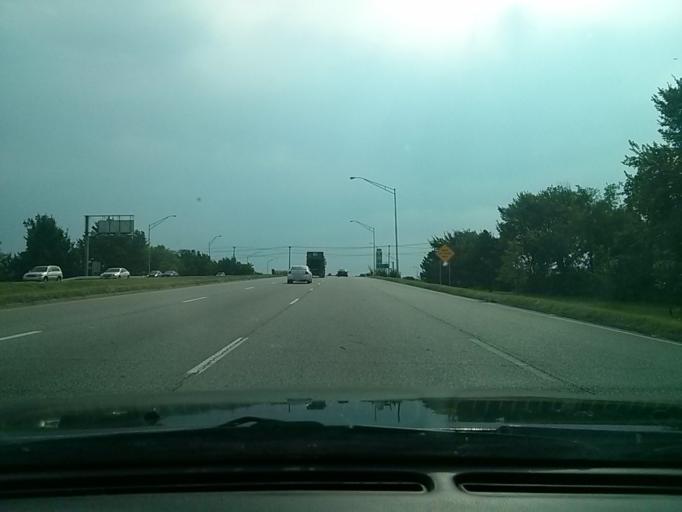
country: US
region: Oklahoma
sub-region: Tulsa County
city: Tulsa
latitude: 36.1427
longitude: -95.9606
